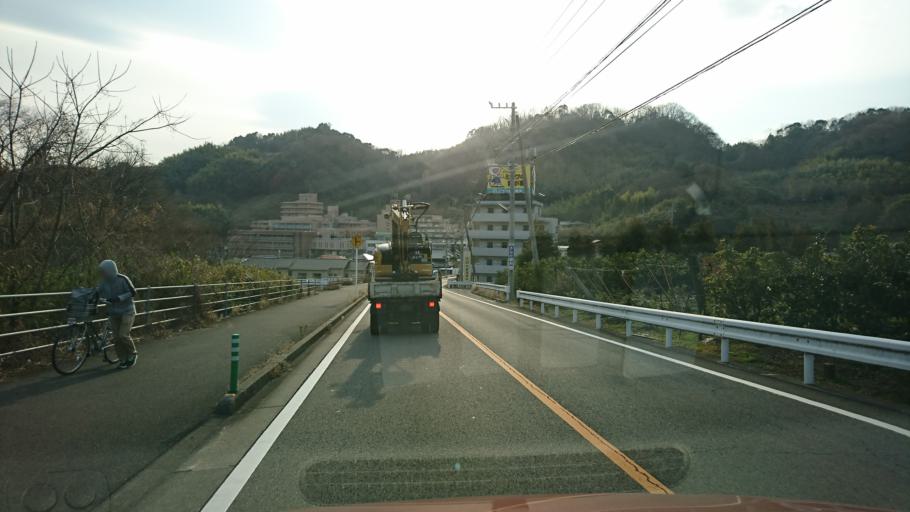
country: JP
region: Ehime
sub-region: Shikoku-chuo Shi
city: Matsuyama
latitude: 33.8663
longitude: 132.7753
